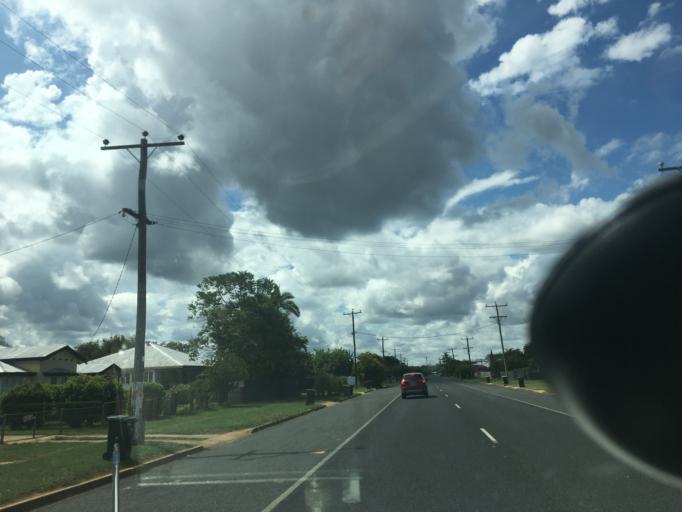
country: AU
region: Queensland
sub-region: Tablelands
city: Mareeba
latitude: -17.0003
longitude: 145.4246
